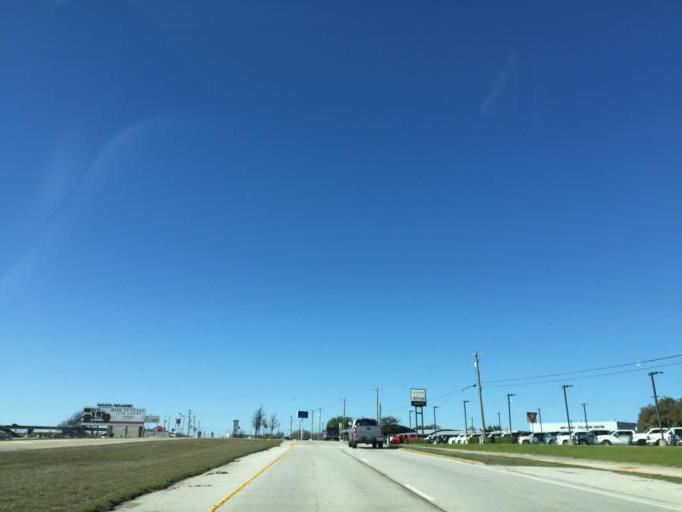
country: US
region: Texas
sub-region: Parker County
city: Hudson Oaks
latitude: 32.7540
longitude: -97.6905
